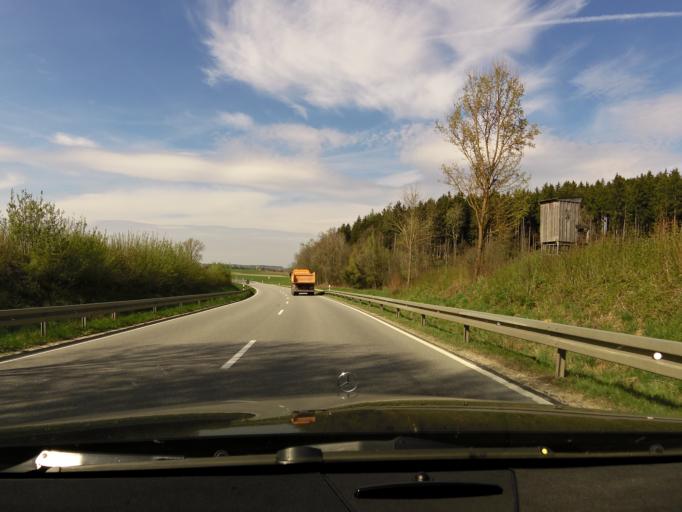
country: DE
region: Bavaria
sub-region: Upper Palatinate
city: Schierling
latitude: 48.7977
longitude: 12.1725
